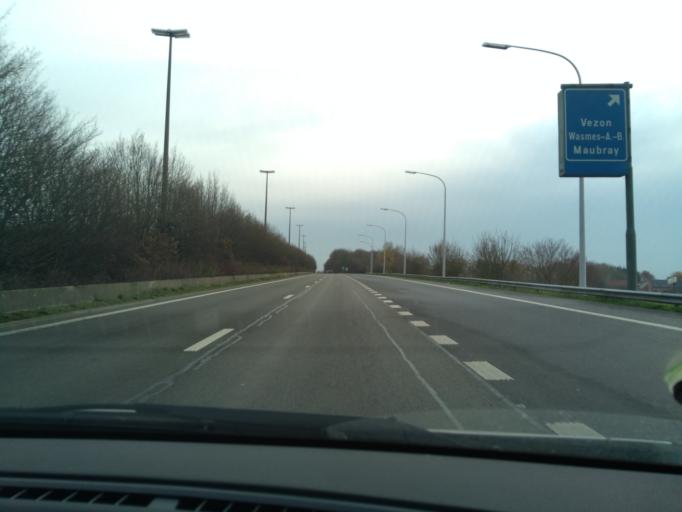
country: BE
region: Wallonia
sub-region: Province du Hainaut
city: Antoing
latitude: 50.5543
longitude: 3.5089
